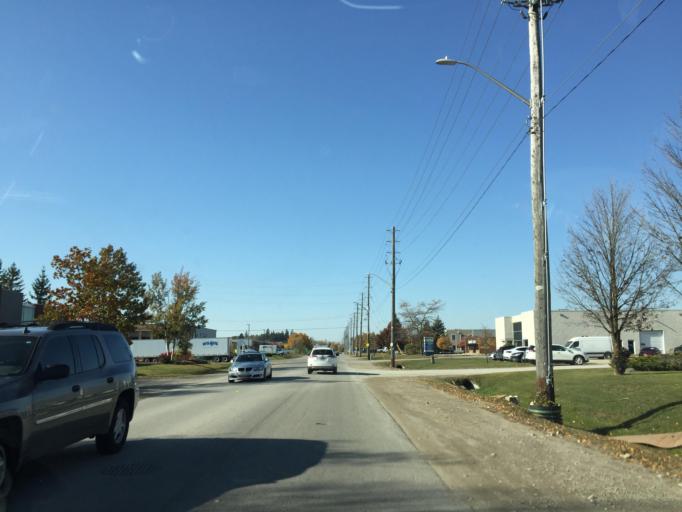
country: CA
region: Ontario
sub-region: Wellington County
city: Guelph
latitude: 43.5550
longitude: -80.2946
